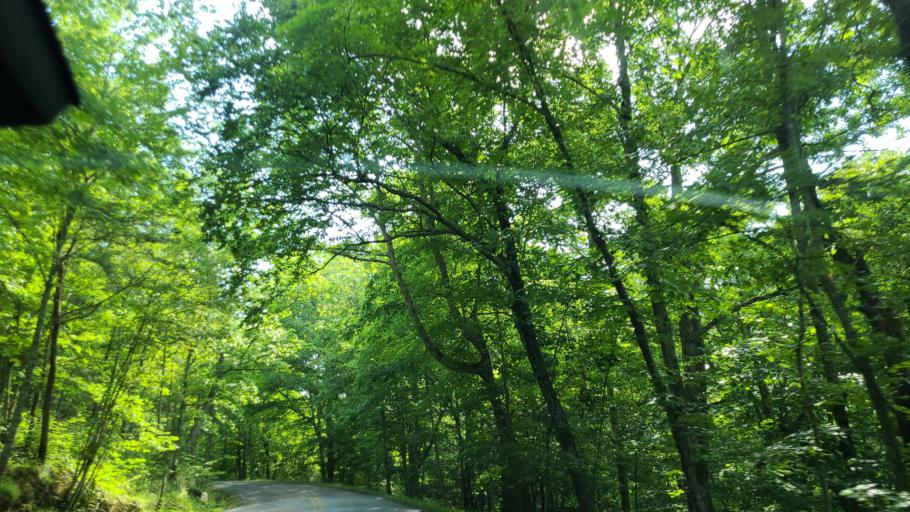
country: US
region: Kentucky
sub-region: Bell County
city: Pineville
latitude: 36.7422
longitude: -83.7134
